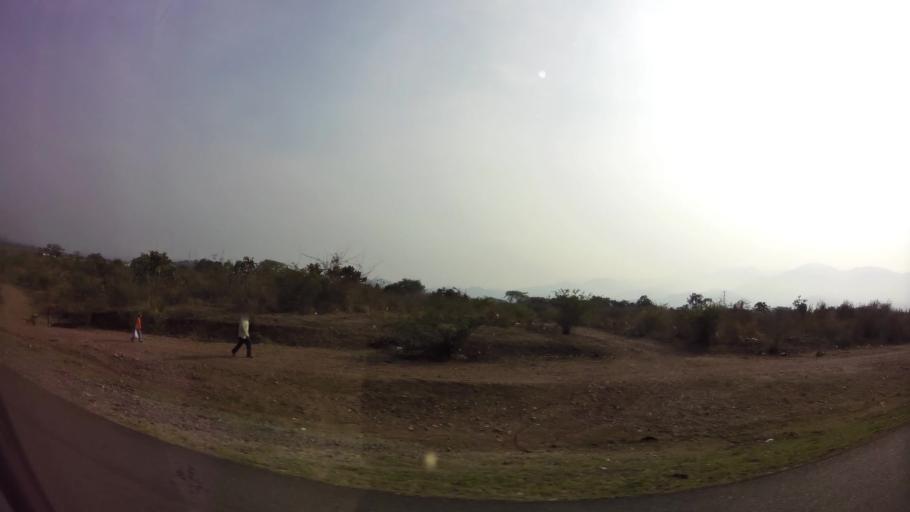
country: HN
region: Comayagua
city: Comayagua
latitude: 14.4290
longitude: -87.6412
